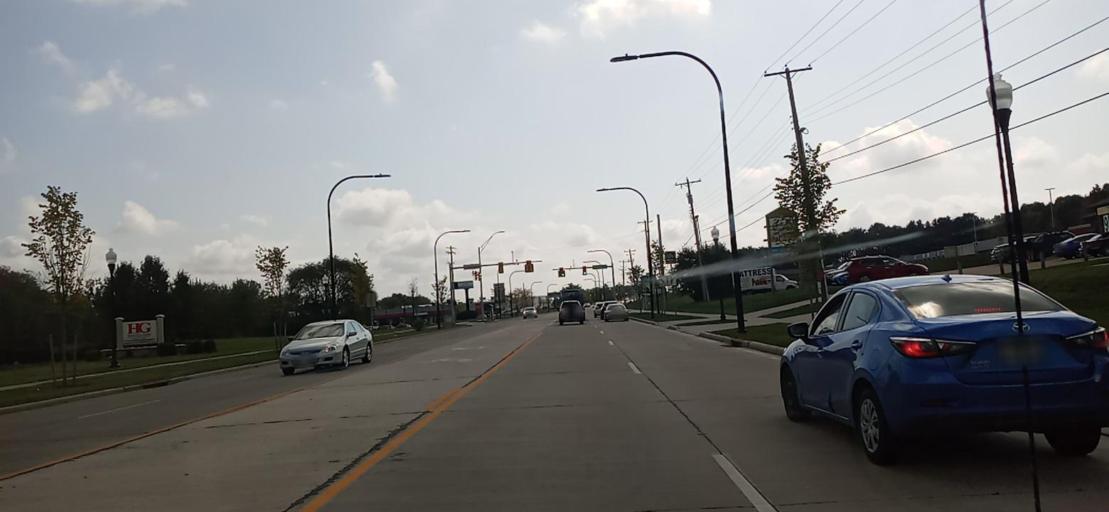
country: US
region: Ohio
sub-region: Summit County
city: Barberton
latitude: 41.0579
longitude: -81.5814
